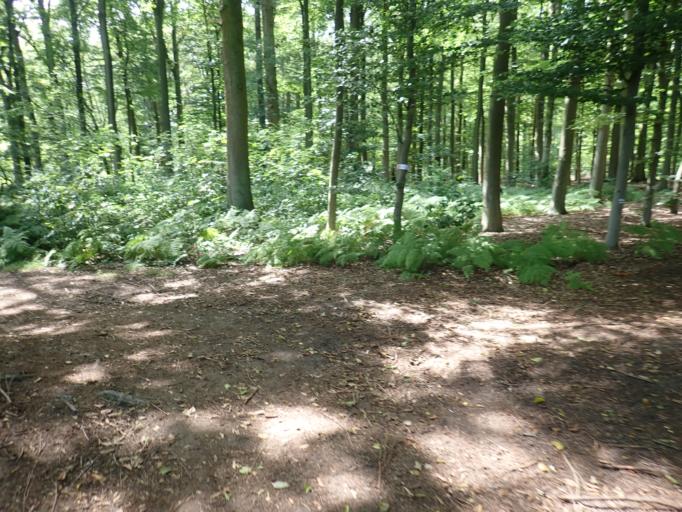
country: BE
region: Flanders
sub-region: Provincie Antwerpen
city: Zandhoven
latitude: 51.2040
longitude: 4.6306
